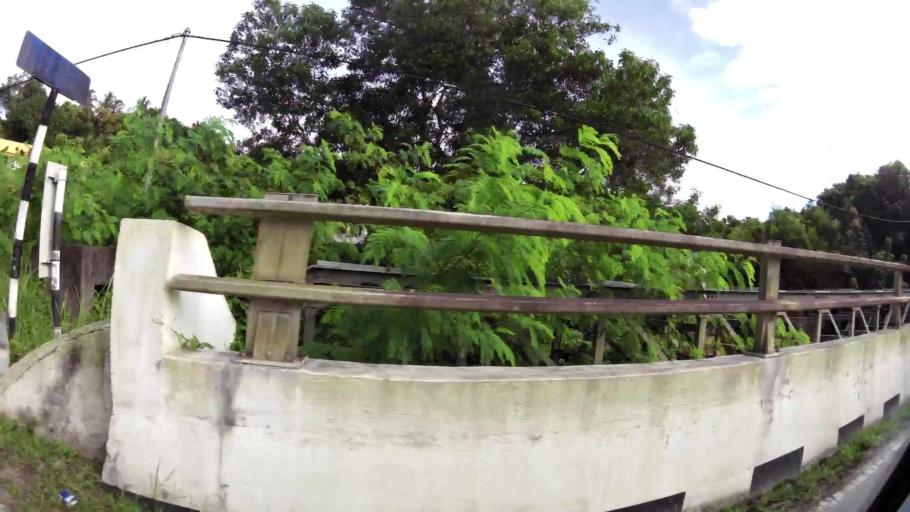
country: BN
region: Brunei and Muara
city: Bandar Seri Begawan
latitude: 4.8853
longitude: 114.9555
